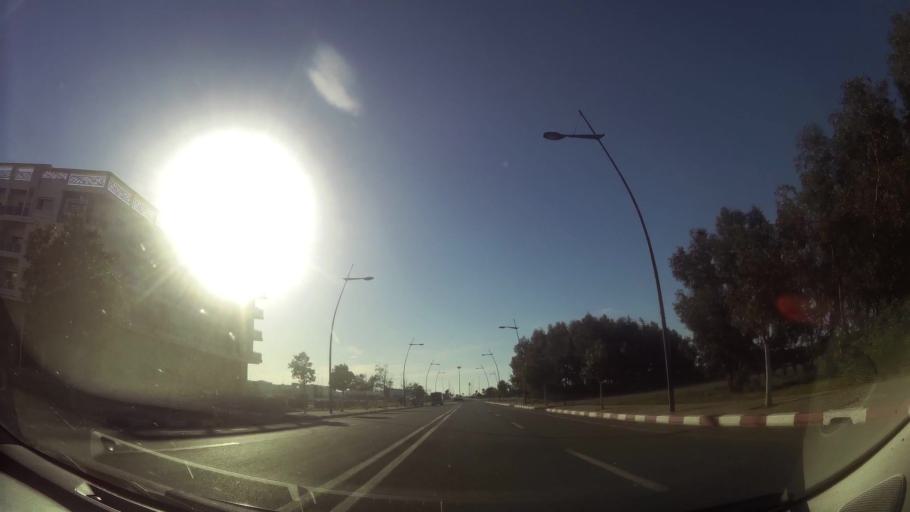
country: MA
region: Oriental
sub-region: Berkane-Taourirt
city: Madagh
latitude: 35.0930
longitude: -2.2572
